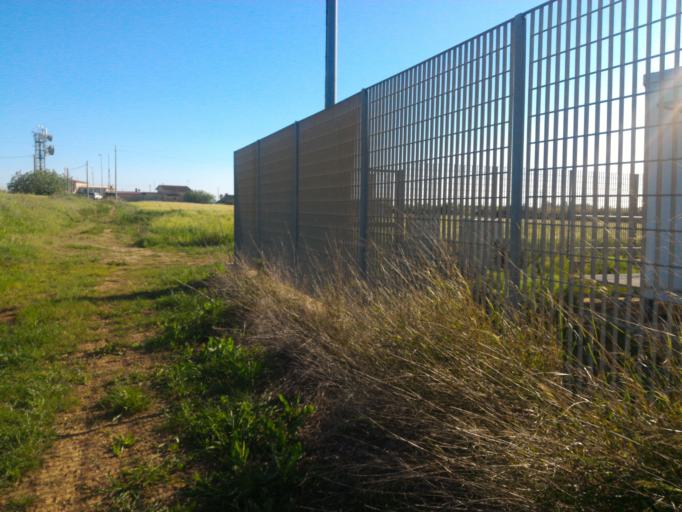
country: IT
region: Calabria
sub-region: Provincia di Crotone
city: Crotone
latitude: 39.0332
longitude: 17.1601
